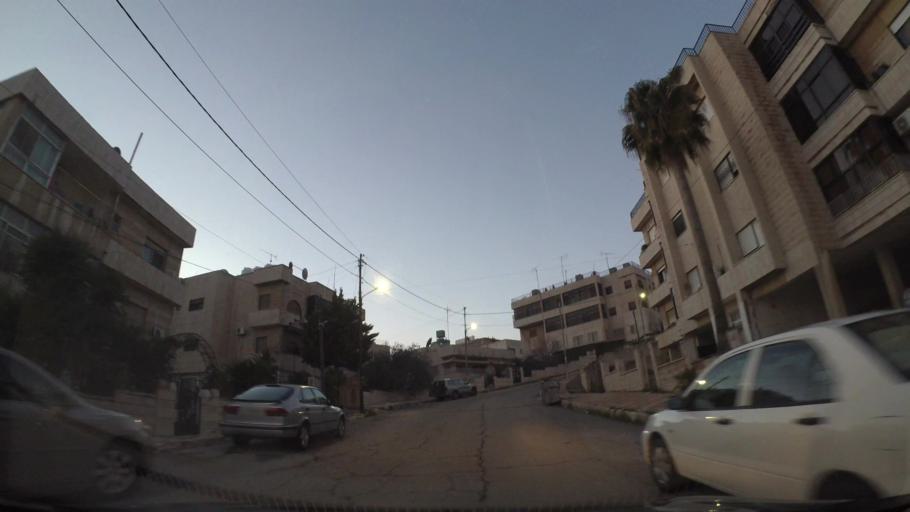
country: JO
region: Amman
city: Al Jubayhah
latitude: 31.9846
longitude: 35.8909
